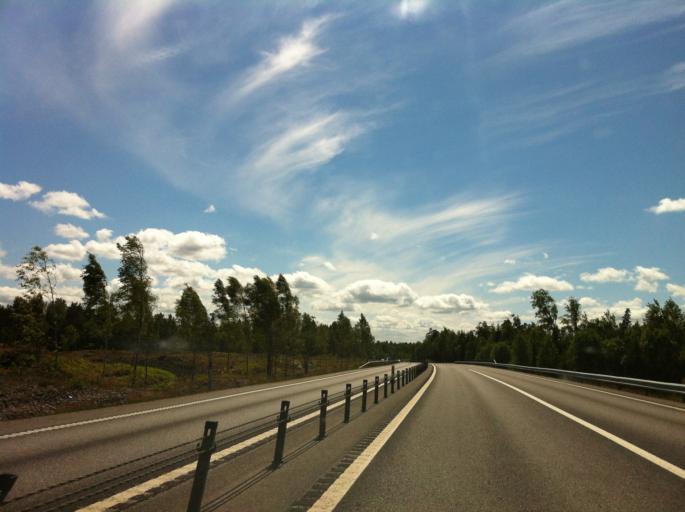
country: SE
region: Vaestra Goetaland
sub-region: Vanersborgs Kommun
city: Vanersborg
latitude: 58.3907
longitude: 12.2917
